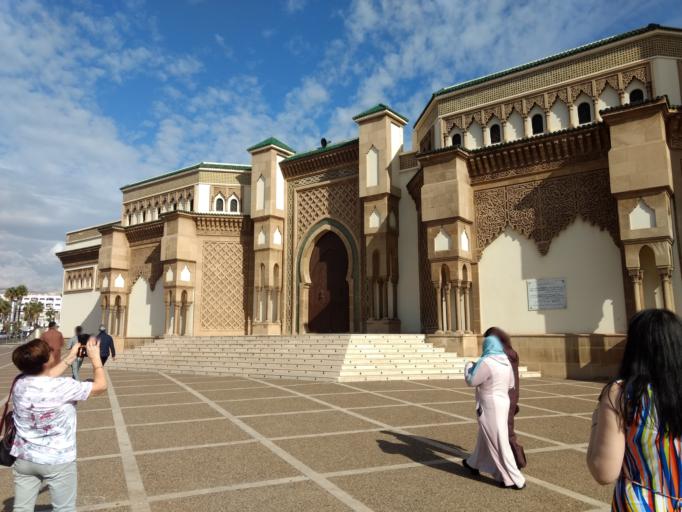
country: MA
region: Souss-Massa-Draa
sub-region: Agadir-Ida-ou-Tnan
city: Agadir
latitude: 30.4222
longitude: -9.5931
